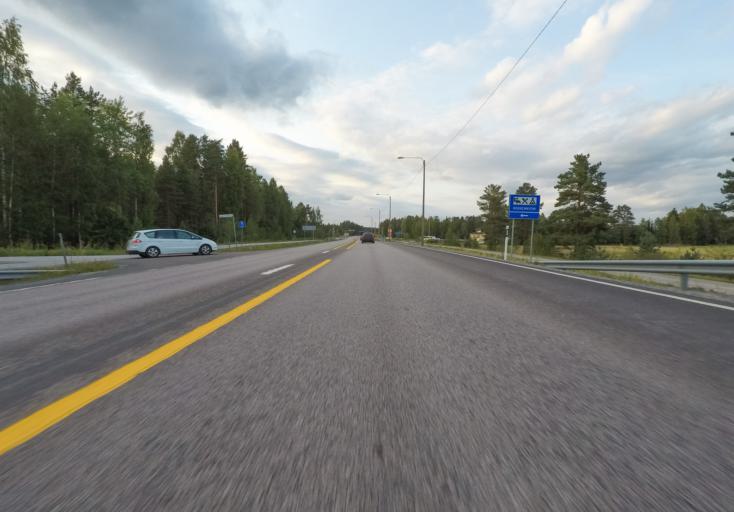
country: FI
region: Paijanne Tavastia
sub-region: Lahti
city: Hartola
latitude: 61.5619
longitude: 26.0057
